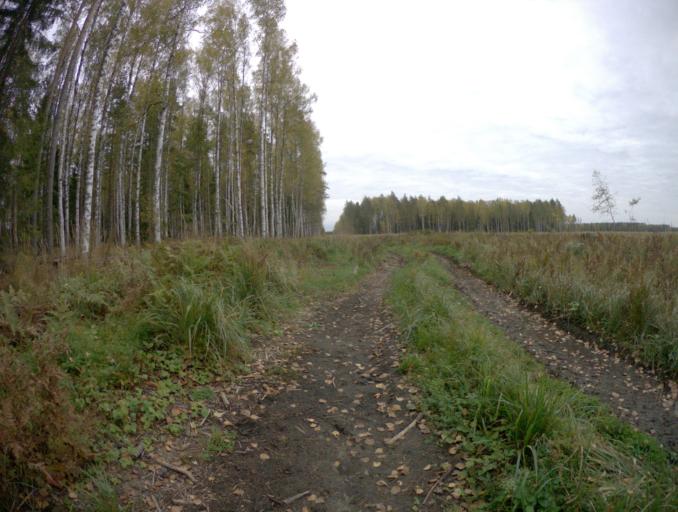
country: RU
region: Vladimir
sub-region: Kovrovskiy Rayon
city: Kovrov
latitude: 56.3159
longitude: 41.5527
